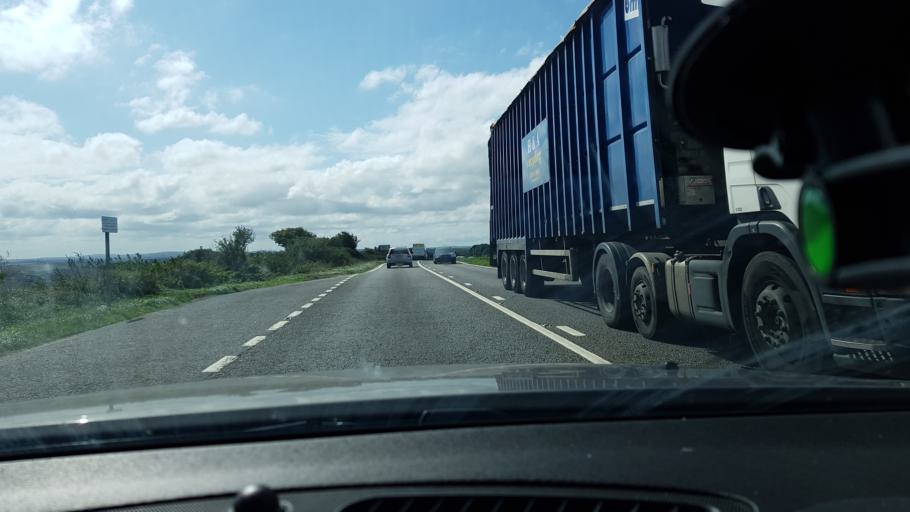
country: GB
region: England
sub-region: Cornwall
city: Truro
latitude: 50.3388
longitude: -5.0500
